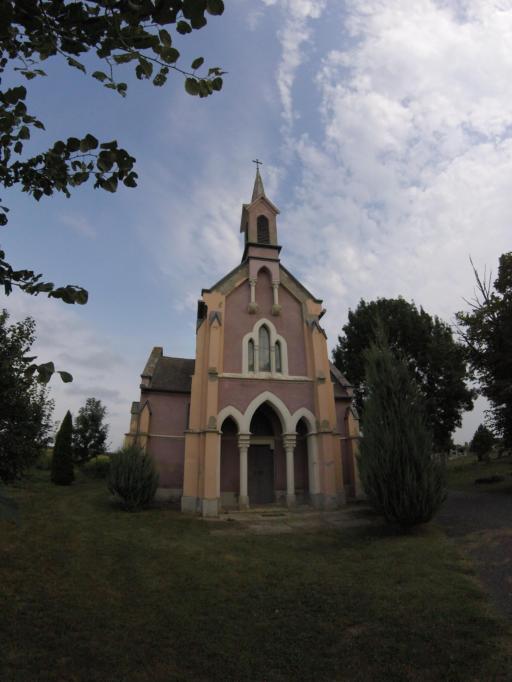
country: HU
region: Veszprem
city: Papa
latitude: 47.3351
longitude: 17.3519
